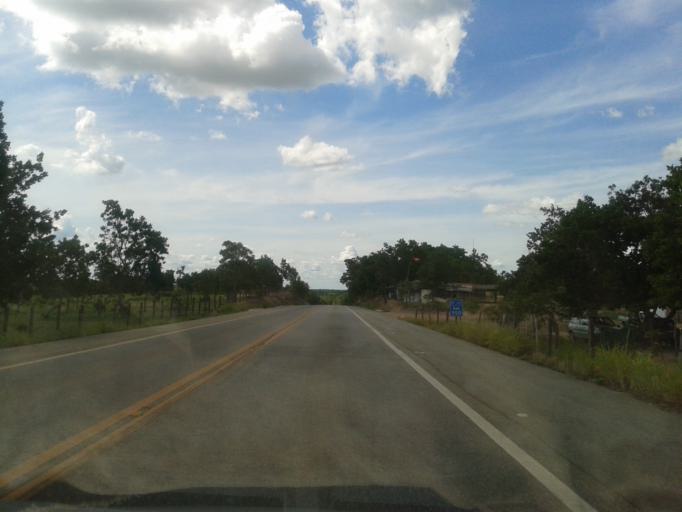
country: BR
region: Goias
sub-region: Itapuranga
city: Itapuranga
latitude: -15.4907
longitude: -50.3219
